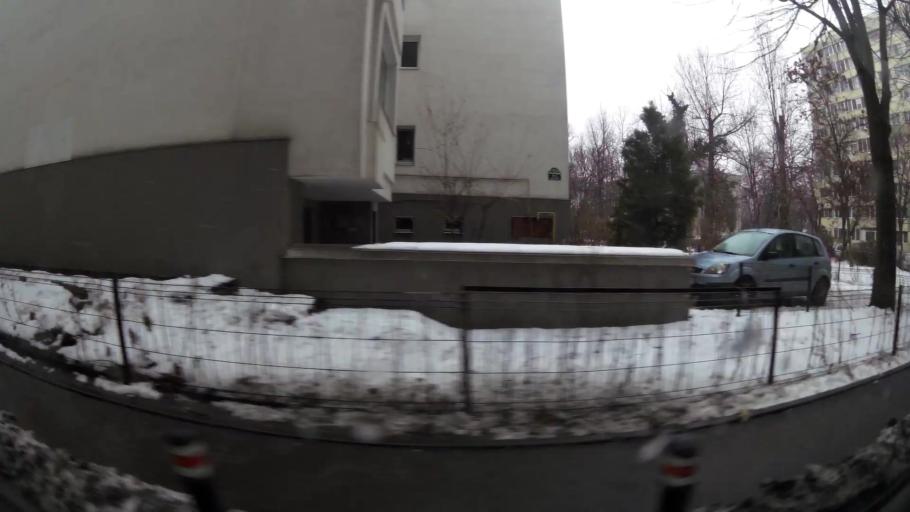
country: RO
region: Ilfov
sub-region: Comuna Chiajna
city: Rosu
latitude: 44.4825
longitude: 26.0573
